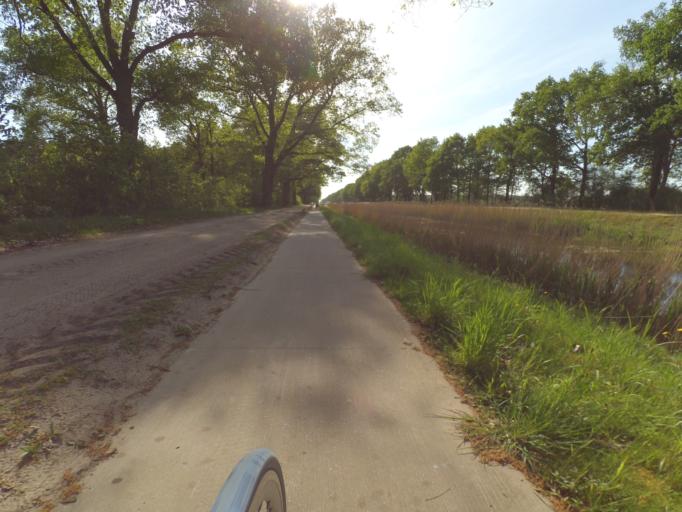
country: NL
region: Overijssel
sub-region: Gemeente Oldenzaal
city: Oldenzaal
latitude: 52.3855
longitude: 6.9443
